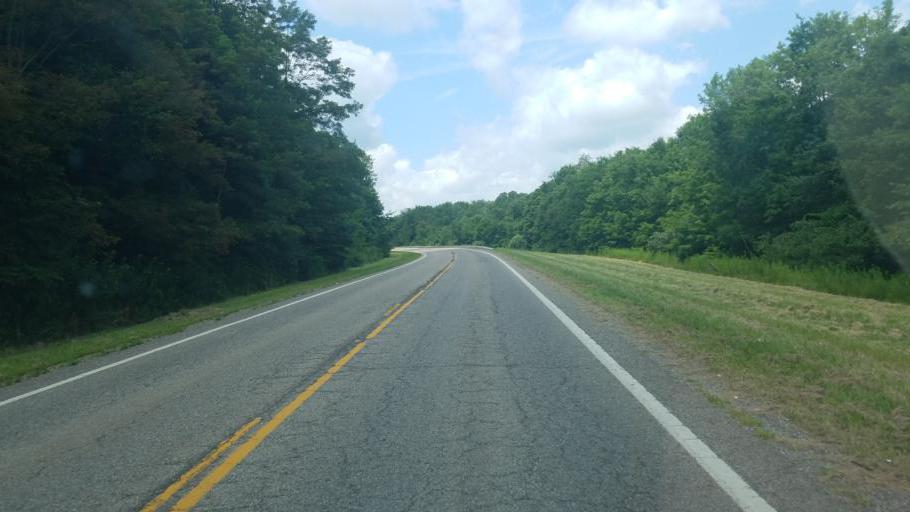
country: US
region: Ohio
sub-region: Columbiana County
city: New Waterford
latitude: 40.7961
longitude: -80.6482
